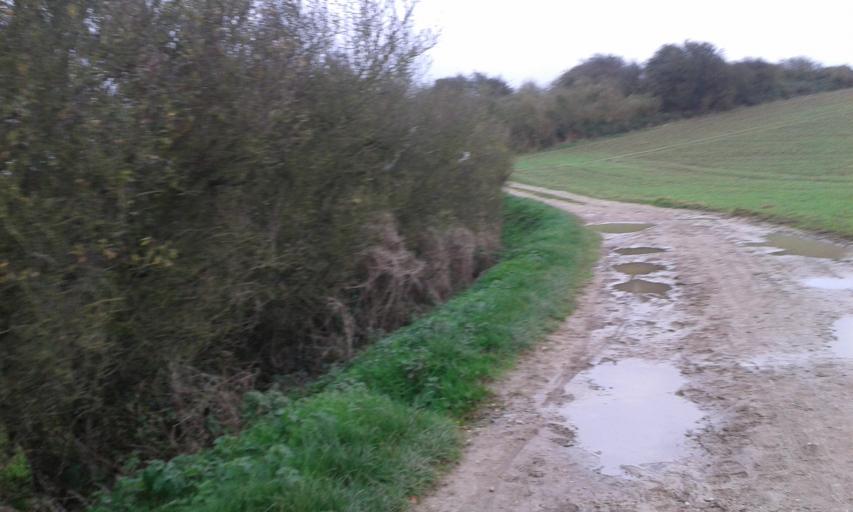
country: FR
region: Nord-Pas-de-Calais
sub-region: Departement du Pas-de-Calais
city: Wissant
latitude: 50.8851
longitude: 1.6938
